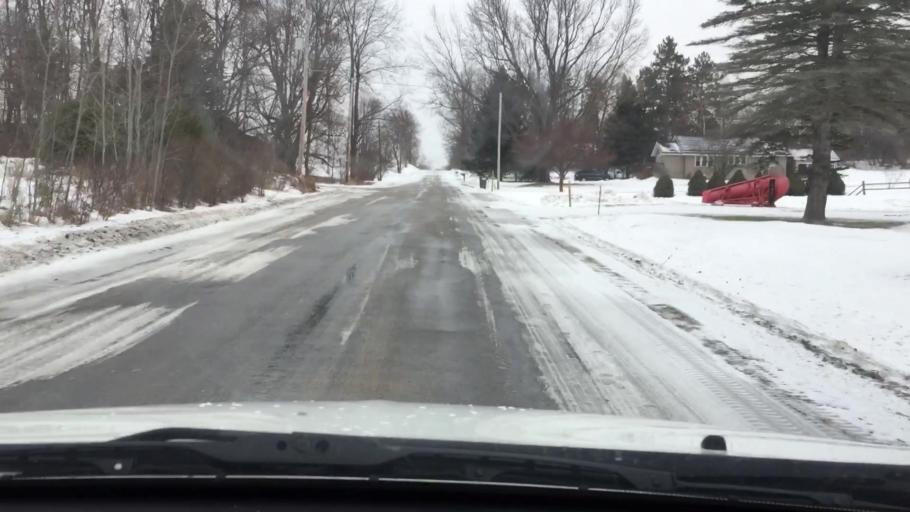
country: US
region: Michigan
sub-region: Osceola County
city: Reed City
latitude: 44.0351
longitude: -85.4539
